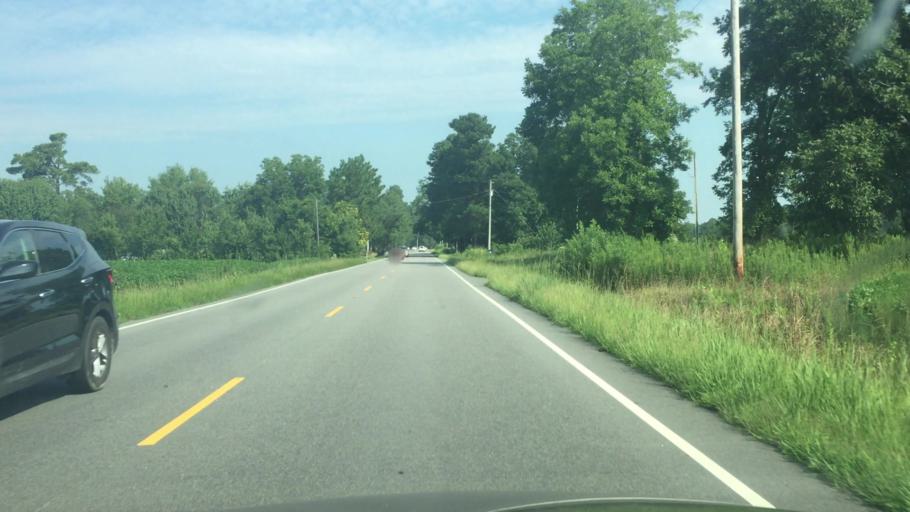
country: US
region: North Carolina
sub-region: Columbus County
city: Chadbourn
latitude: 34.2875
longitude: -78.8223
